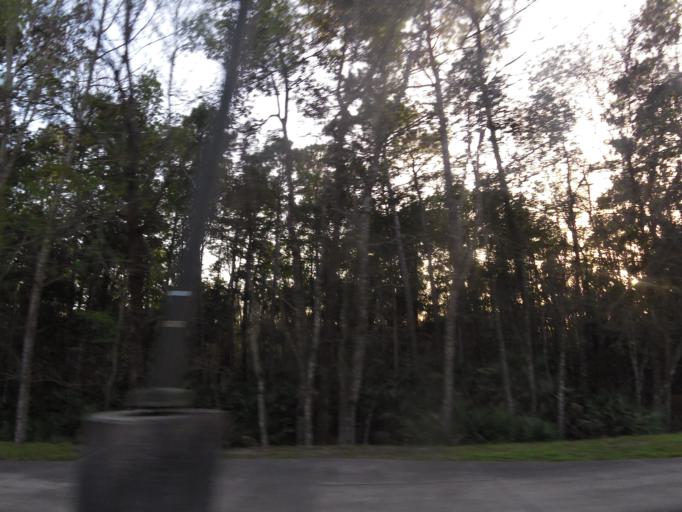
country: US
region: Florida
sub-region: Duval County
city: Jacksonville Beach
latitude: 30.2642
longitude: -81.5101
